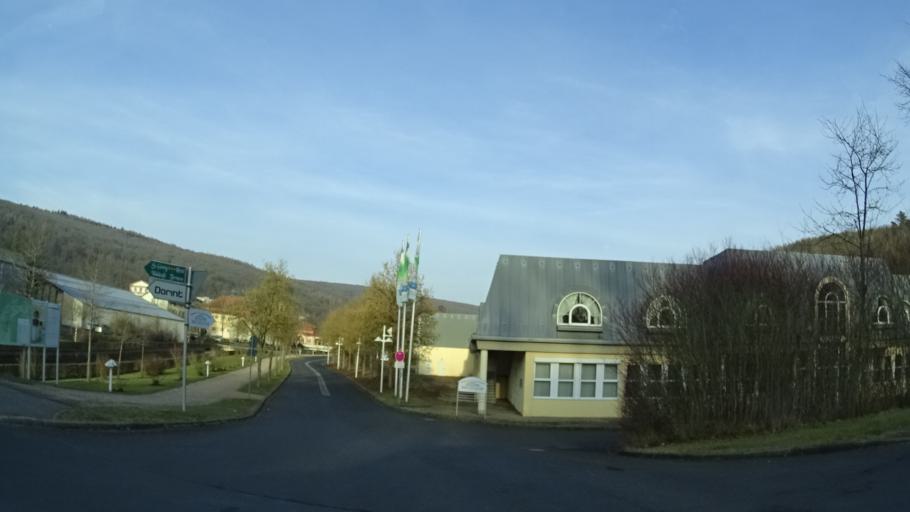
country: DE
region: Bavaria
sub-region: Regierungsbezirk Unterfranken
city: Bad Bruckenau
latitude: 50.3009
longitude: 9.7468
